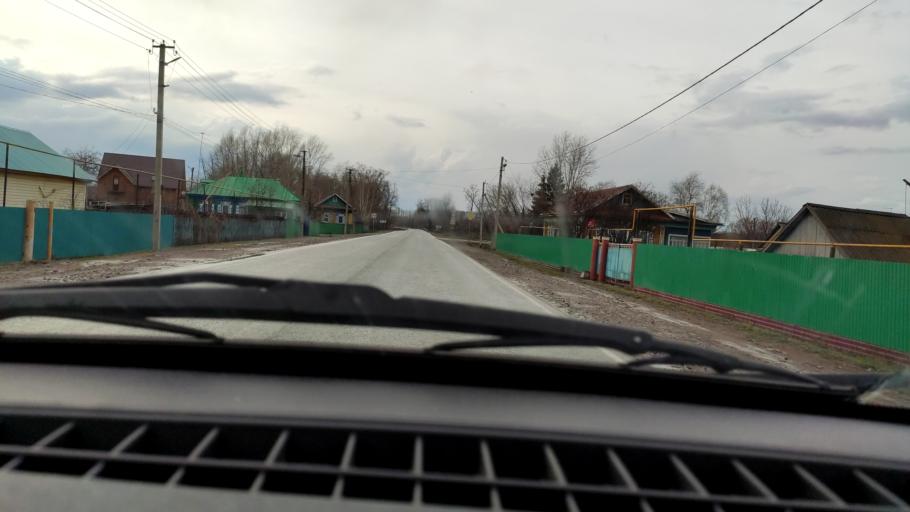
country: RU
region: Bashkortostan
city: Alekseyevka
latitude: 55.0741
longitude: 55.0820
